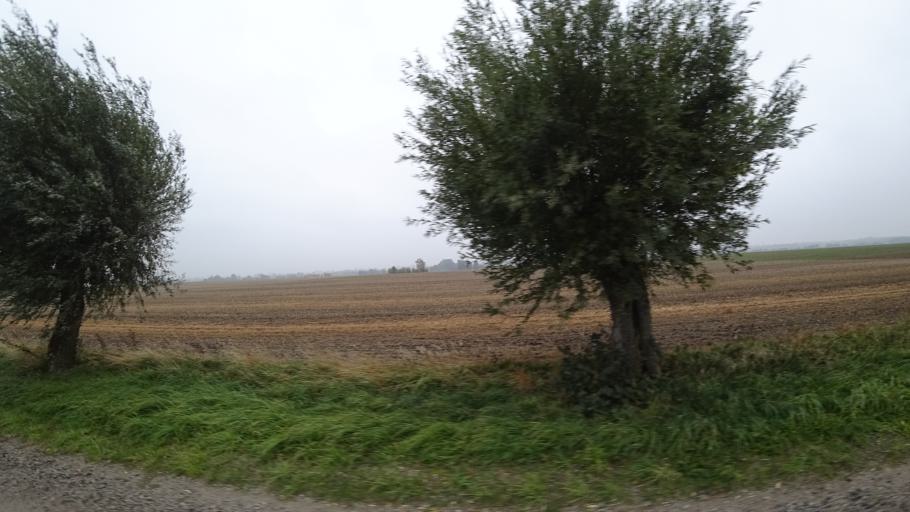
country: SE
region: Skane
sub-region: Kavlinge Kommun
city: Kaevlinge
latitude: 55.8080
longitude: 13.1360
